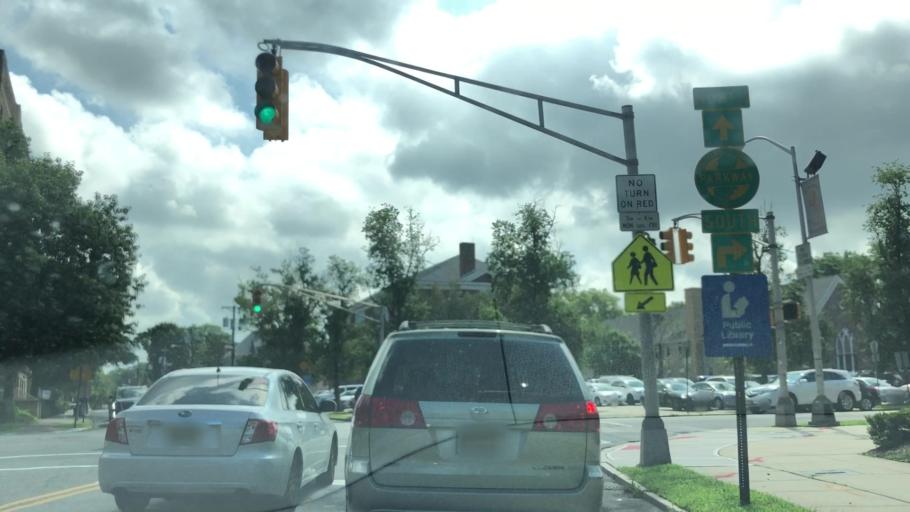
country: US
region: New Jersey
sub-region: Essex County
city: Glen Ridge
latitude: 40.7999
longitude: -74.1972
